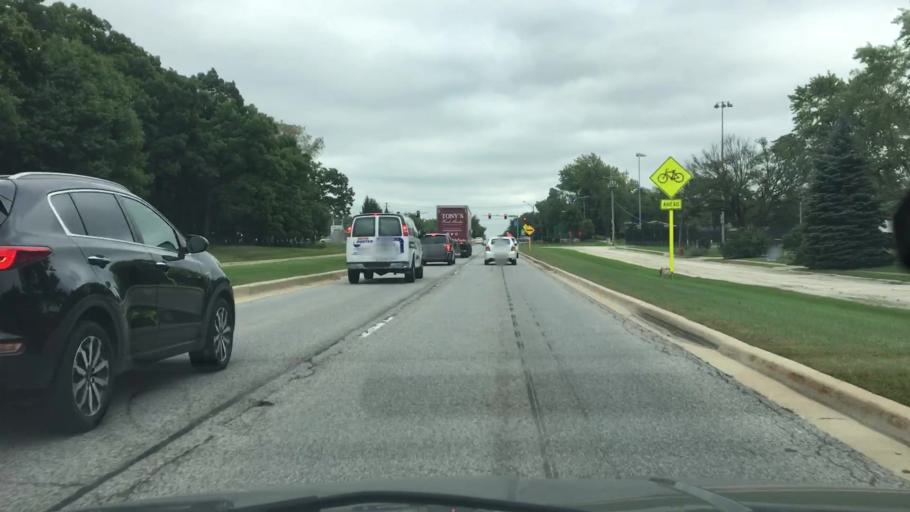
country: US
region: Illinois
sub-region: DuPage County
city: Woodridge
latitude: 41.7500
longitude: -88.0546
